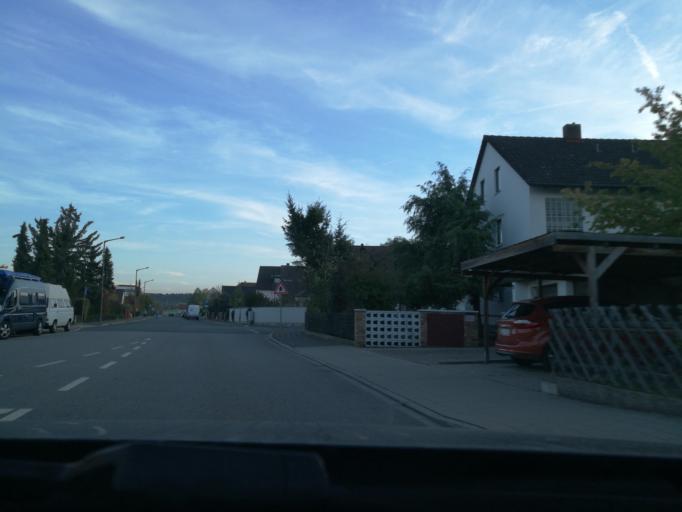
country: DE
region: Bavaria
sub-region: Regierungsbezirk Mittelfranken
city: Seukendorf
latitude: 49.4917
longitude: 10.9161
